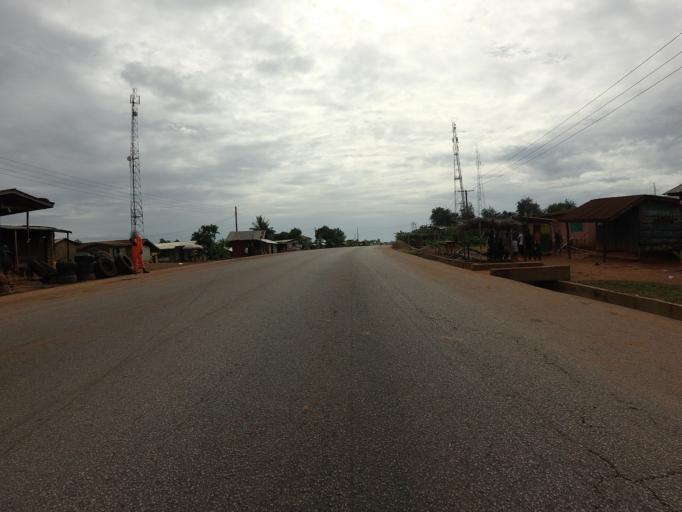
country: GH
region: Eastern
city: Nkawkaw
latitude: 6.5984
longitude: -0.8384
